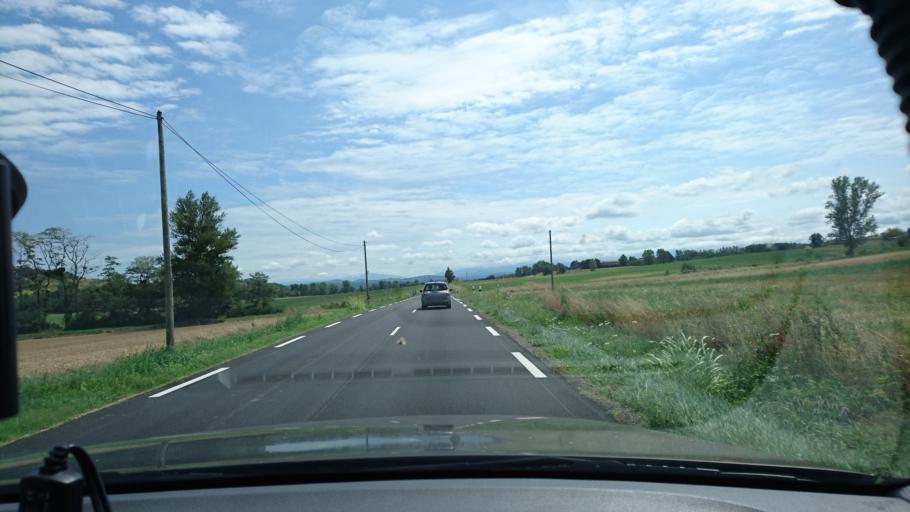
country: FR
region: Midi-Pyrenees
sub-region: Departement de la Haute-Garonne
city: Gaillac-Toulza
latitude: 43.1899
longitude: 1.3967
